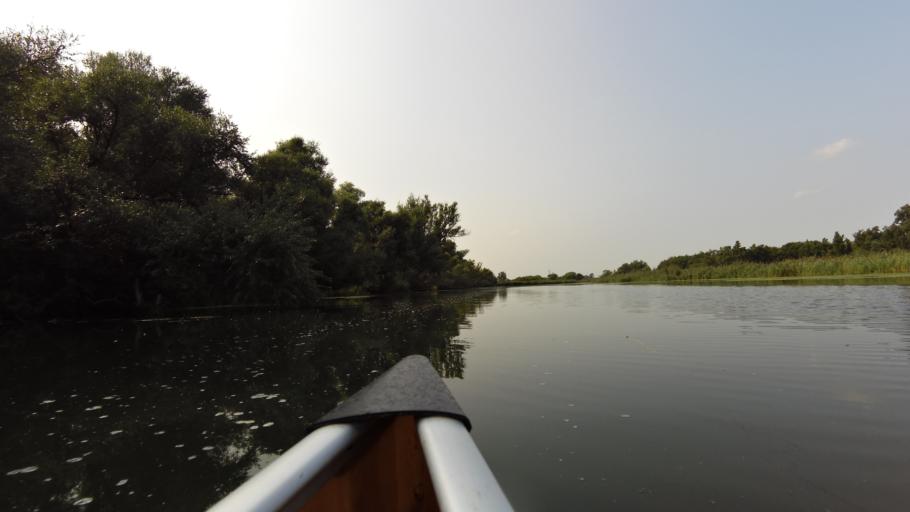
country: NL
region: North Brabant
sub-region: Gemeente Made en Drimmelen
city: Drimmelen
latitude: 51.7571
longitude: 4.8264
